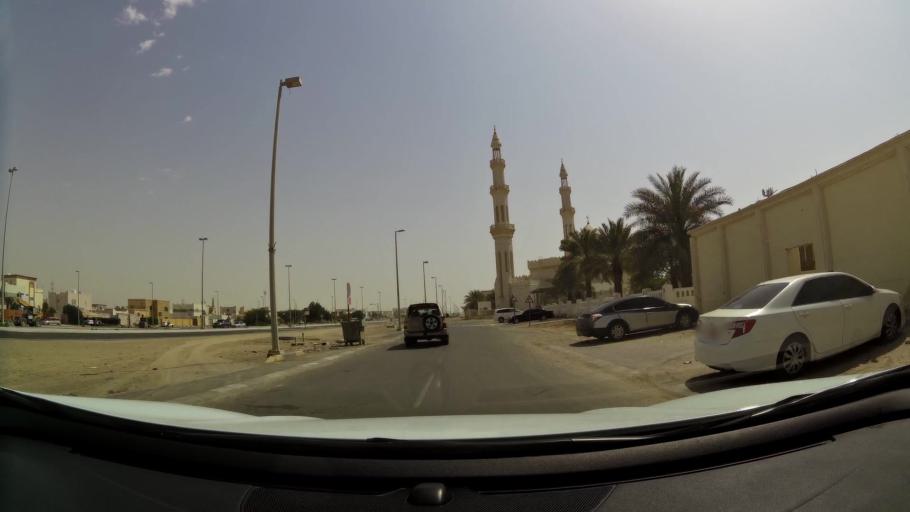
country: AE
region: Abu Dhabi
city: Abu Dhabi
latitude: 24.3012
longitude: 54.6460
